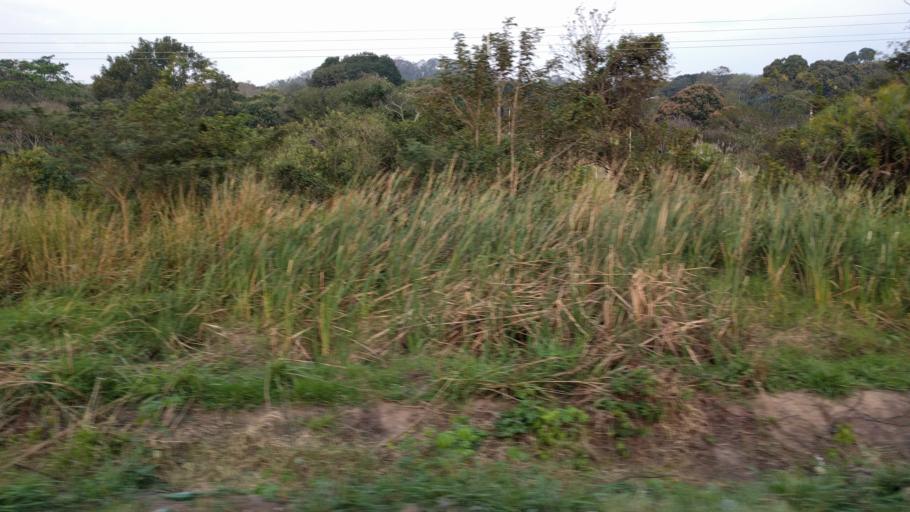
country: BO
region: Santa Cruz
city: Santa Rita
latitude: -17.9524
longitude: -63.3553
